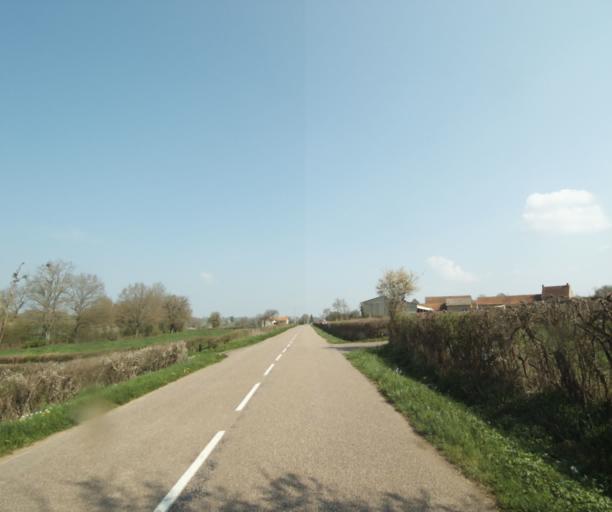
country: FR
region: Bourgogne
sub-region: Departement de Saone-et-Loire
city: Charolles
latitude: 46.4623
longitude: 4.3121
